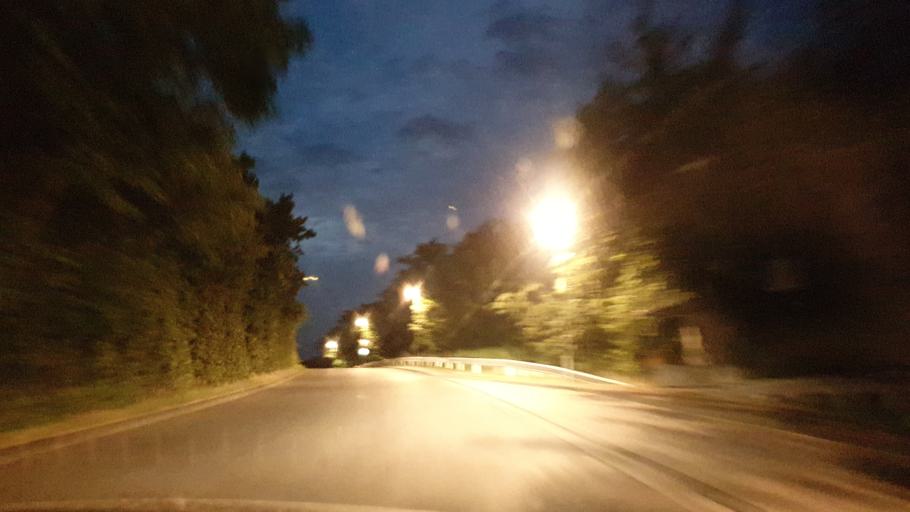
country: DE
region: Rheinland-Pfalz
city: Andernach
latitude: 50.4163
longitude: 7.4103
